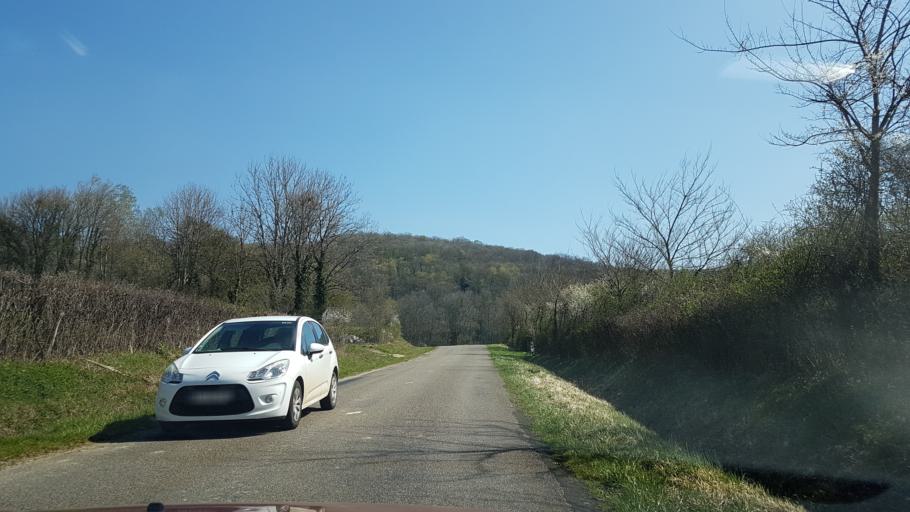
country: FR
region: Bourgogne
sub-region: Departement de Saone-et-Loire
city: Cuiseaux
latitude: 46.4821
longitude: 5.4694
